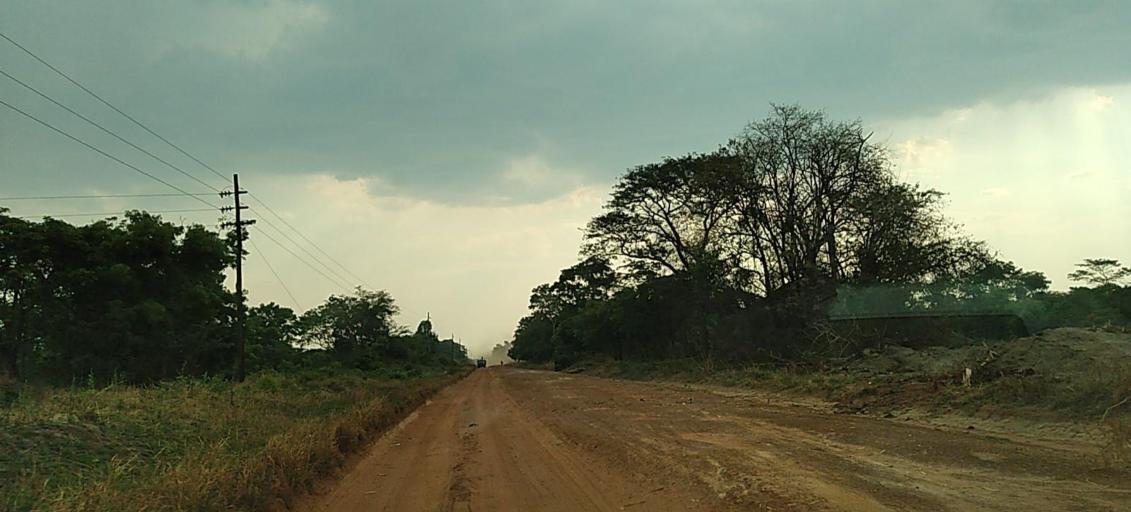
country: ZM
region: Copperbelt
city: Kalulushi
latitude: -12.9412
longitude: 27.9224
